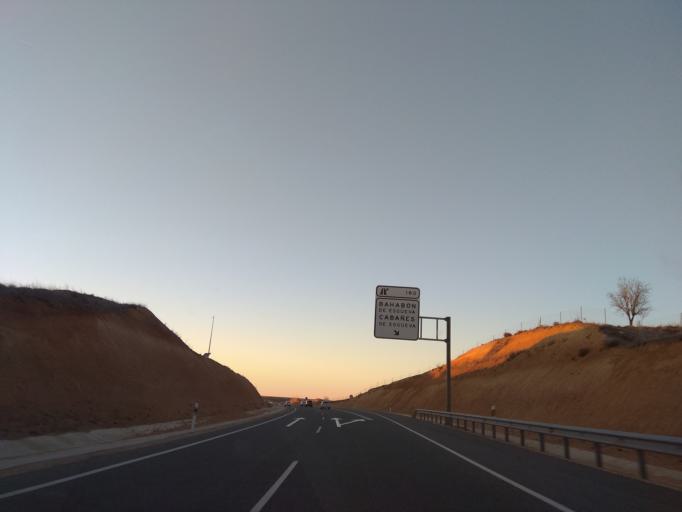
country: ES
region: Castille and Leon
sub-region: Provincia de Burgos
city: Bahabon de Esgueva
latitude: 41.8484
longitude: -3.7192
